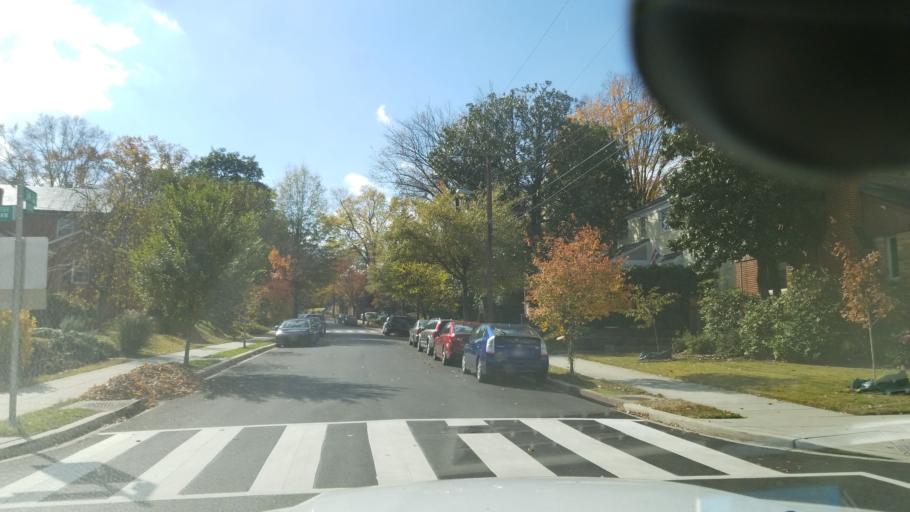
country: US
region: Maryland
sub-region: Montgomery County
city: Chevy Chase Village
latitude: 38.9561
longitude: -77.0668
